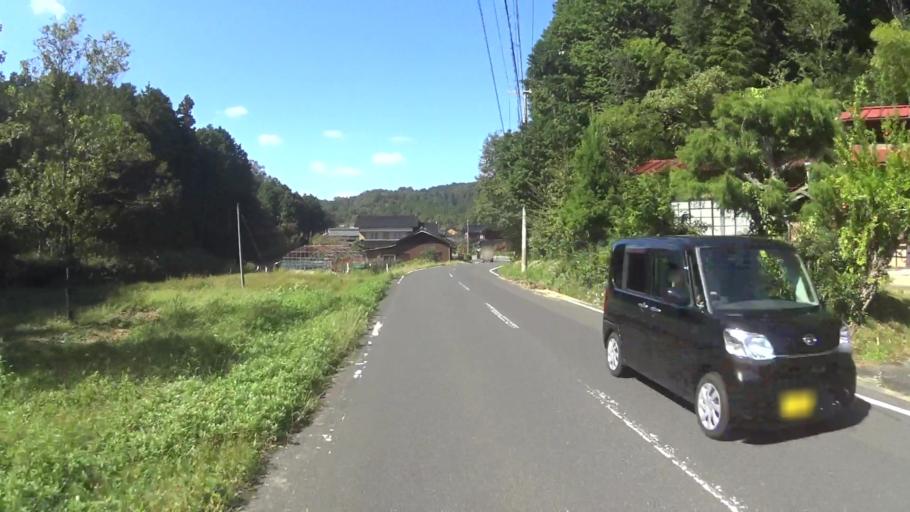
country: JP
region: Hyogo
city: Toyooka
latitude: 35.5947
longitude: 134.9482
